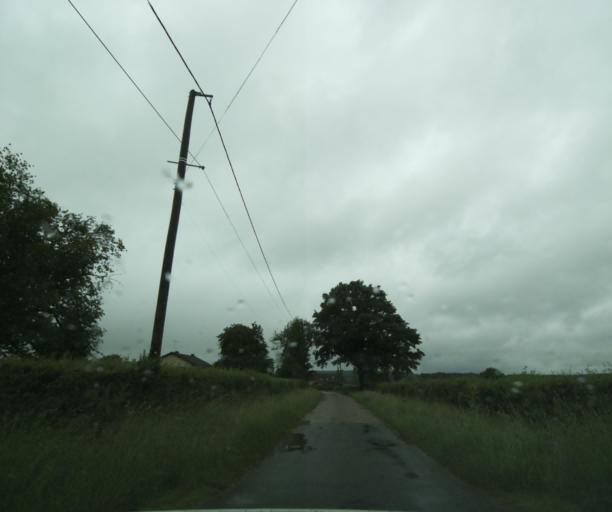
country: FR
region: Bourgogne
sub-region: Departement de Saone-et-Loire
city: Saint-Vallier
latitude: 46.5364
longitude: 4.3936
